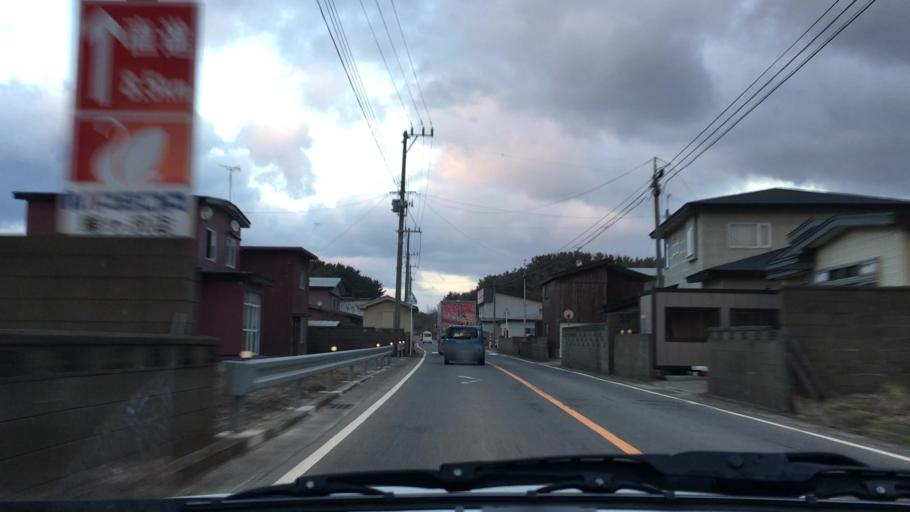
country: JP
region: Aomori
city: Shimokizukuri
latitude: 40.7547
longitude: 140.1506
